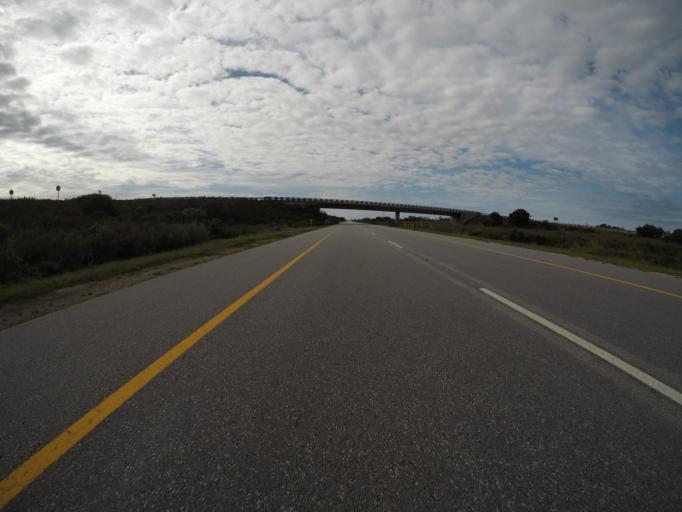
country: ZA
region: Eastern Cape
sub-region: Cacadu District Municipality
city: Kruisfontein
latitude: -34.0065
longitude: 24.7788
